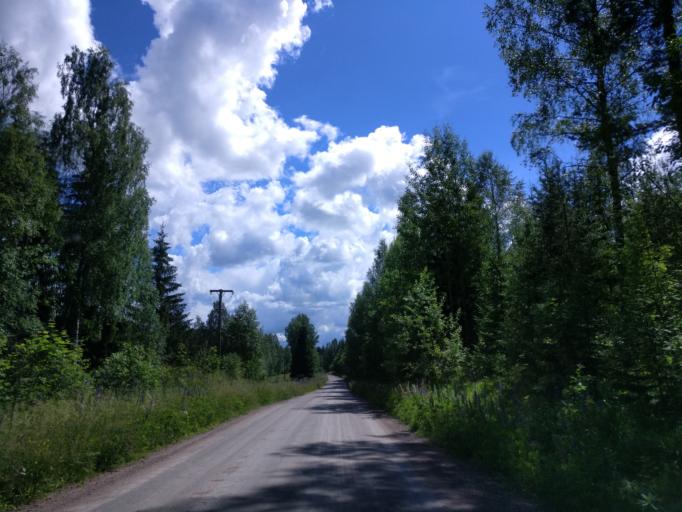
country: SE
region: Vaermland
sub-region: Hagfors Kommun
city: Hagfors
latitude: 60.0428
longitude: 13.6617
